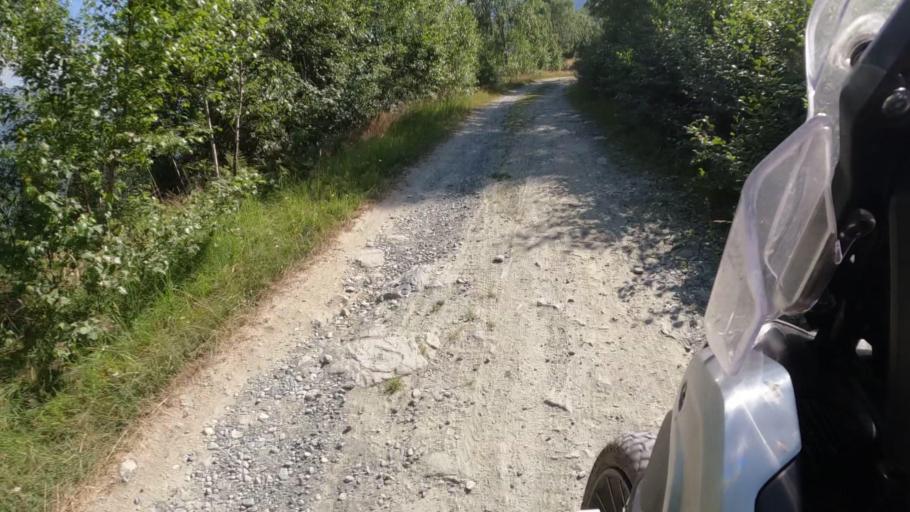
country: IT
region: Piedmont
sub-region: Provincia di Torino
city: Lemie
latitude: 45.2024
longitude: 7.3117
